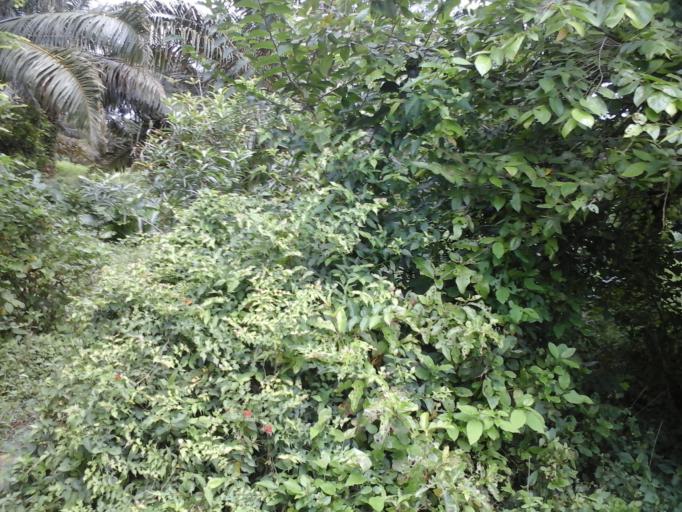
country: CO
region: Bolivar
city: San Pablo
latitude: 10.1619
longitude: -75.2752
